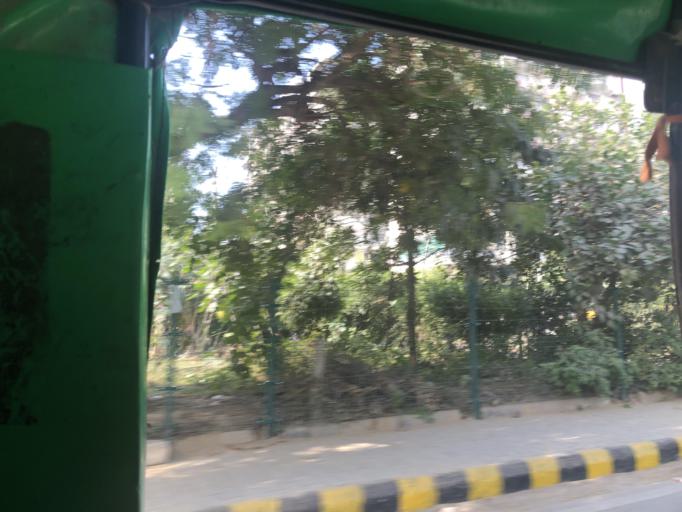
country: IN
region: Haryana
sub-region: Gurgaon
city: Gurgaon
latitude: 28.4356
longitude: 77.0904
